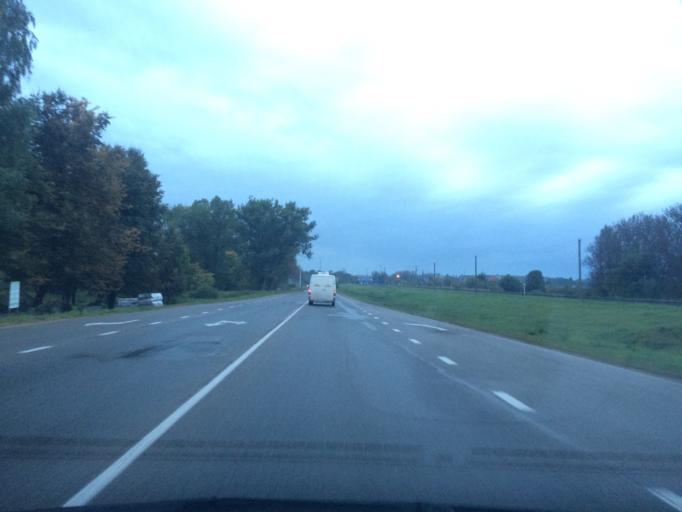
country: LV
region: Jekabpils Rajons
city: Jekabpils
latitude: 56.5120
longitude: 25.8719
